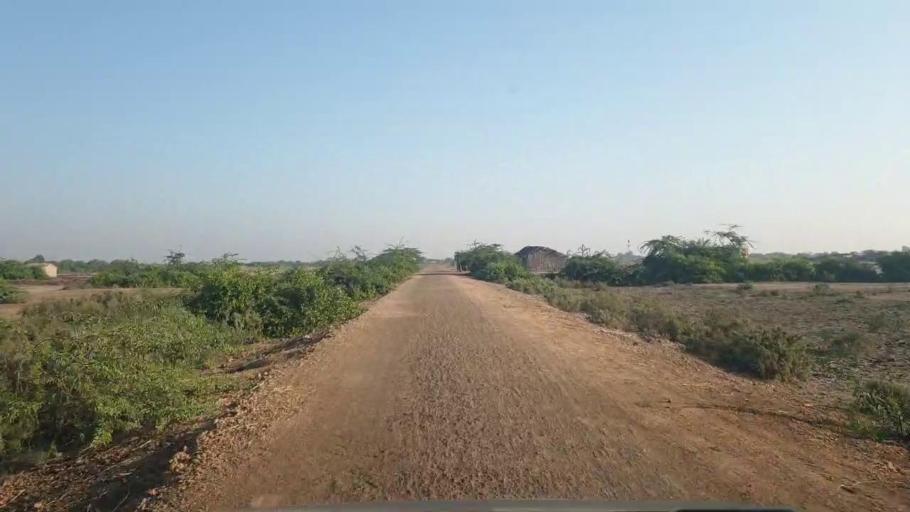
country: PK
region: Sindh
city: Badin
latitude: 24.7251
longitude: 68.8642
